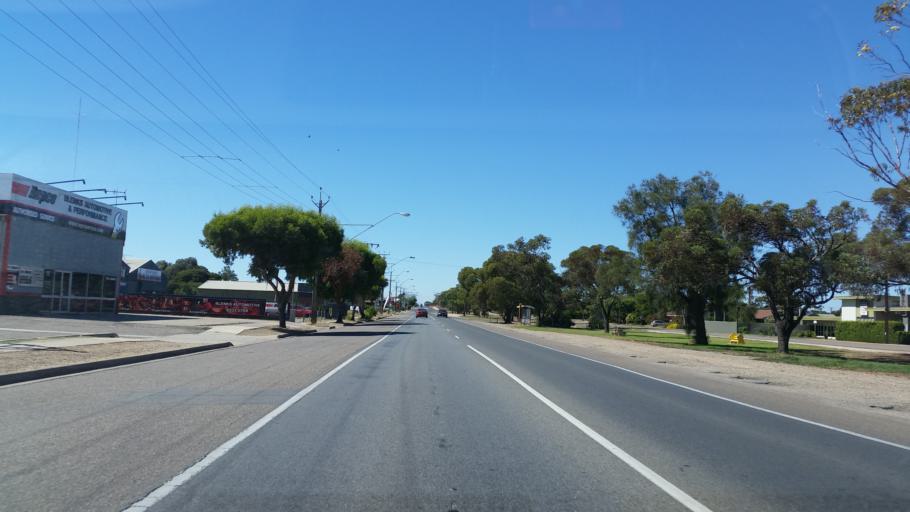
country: AU
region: South Australia
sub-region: Murray Bridge
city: Murray Bridge
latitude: -35.1315
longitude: 139.2451
